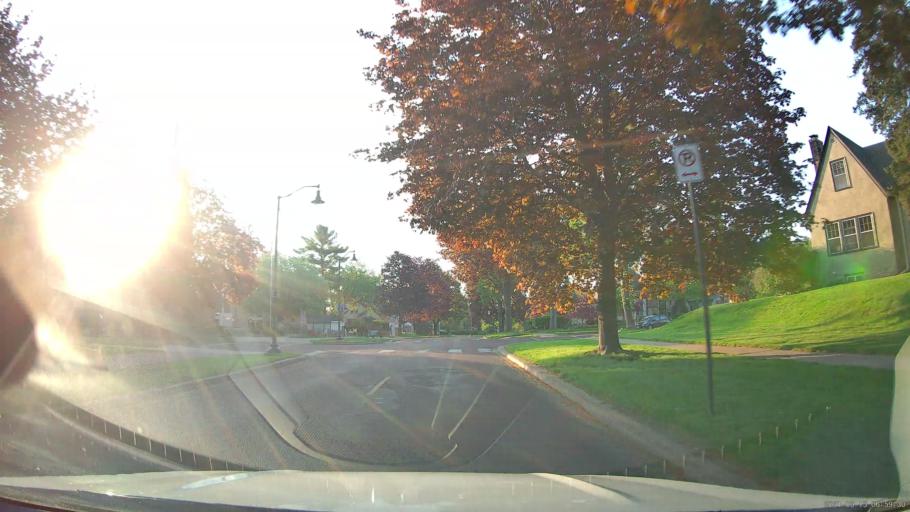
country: US
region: Minnesota
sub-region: Hennepin County
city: Saint Anthony
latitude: 45.0237
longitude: -93.2361
